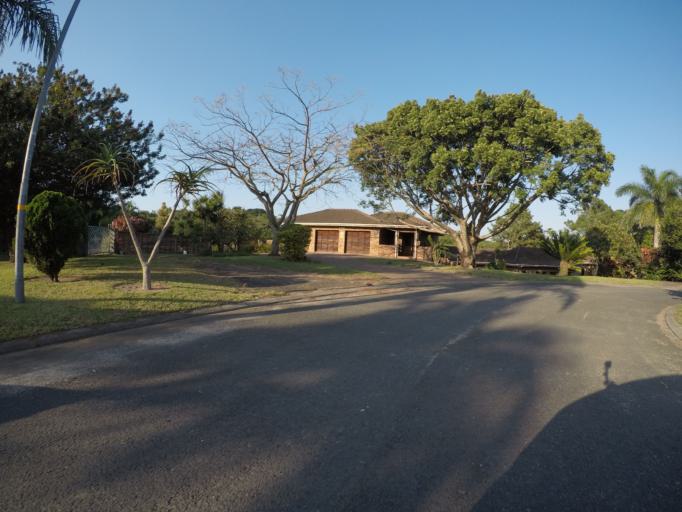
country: ZA
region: KwaZulu-Natal
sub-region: uThungulu District Municipality
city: Richards Bay
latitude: -28.7742
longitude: 32.1143
